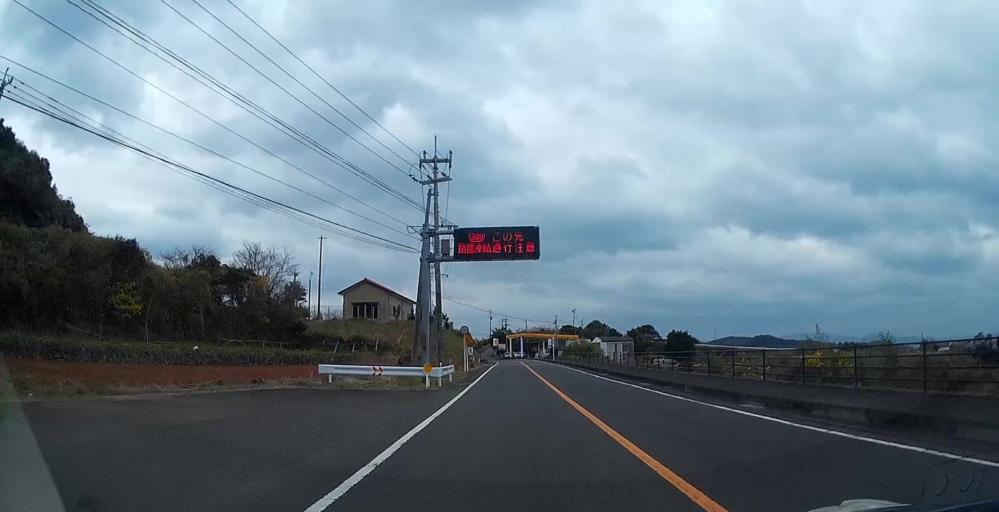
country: JP
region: Kagoshima
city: Akune
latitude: 32.0965
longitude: 130.1635
